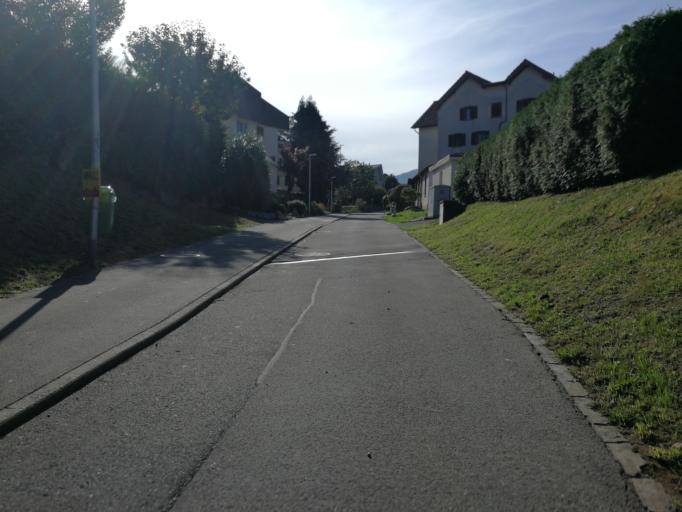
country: CH
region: Schwyz
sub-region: Bezirk Schwyz
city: Goldau
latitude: 47.0551
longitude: 8.5385
